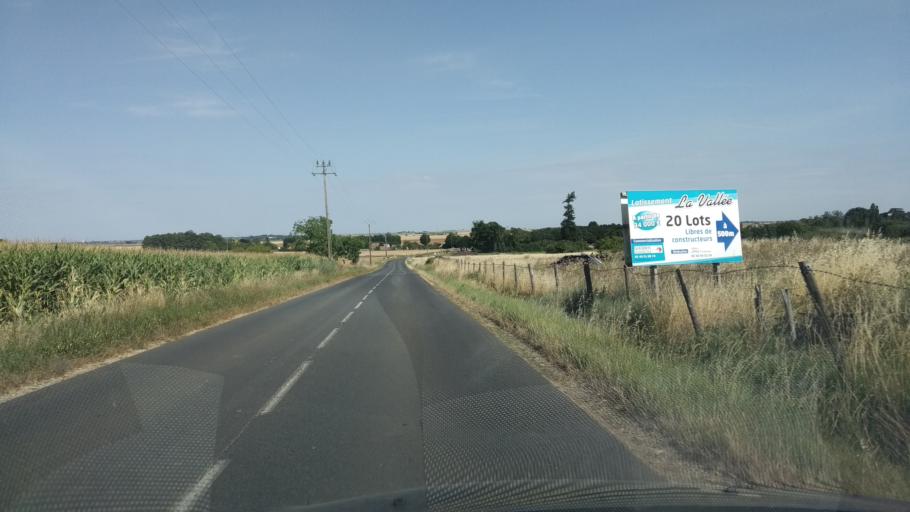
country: FR
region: Poitou-Charentes
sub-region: Departement de la Vienne
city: Vouille
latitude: 46.6820
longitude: 0.1712
